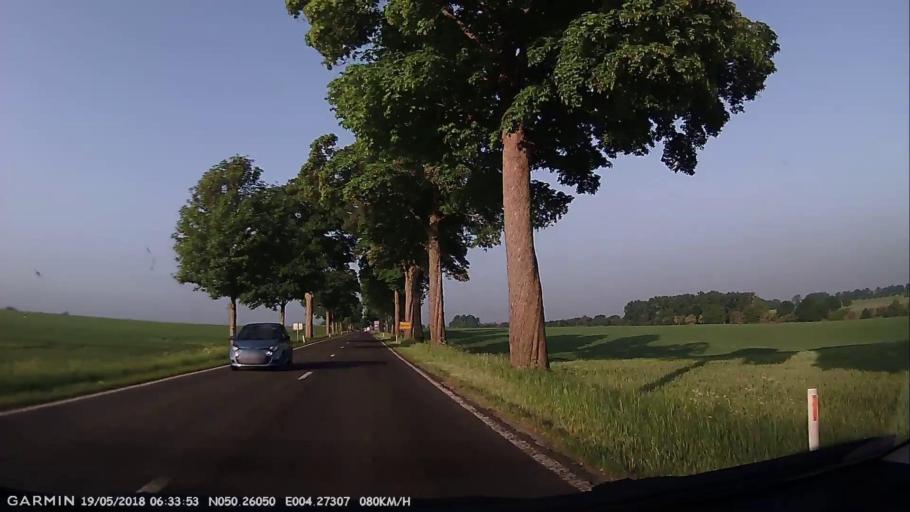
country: BE
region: Wallonia
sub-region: Province du Hainaut
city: Beaumont
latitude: 50.2605
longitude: 4.2731
